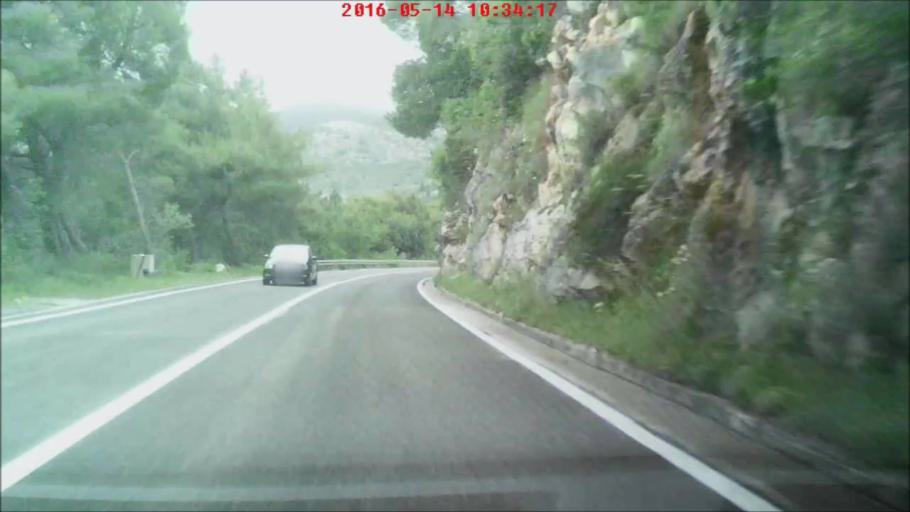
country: HR
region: Dubrovacko-Neretvanska
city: Podgora
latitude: 42.7800
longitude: 17.8906
